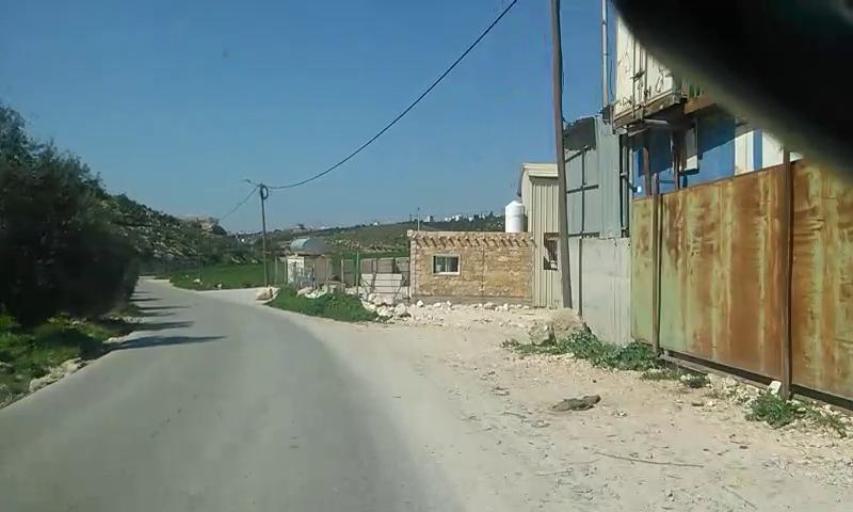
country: PS
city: Bayt Maqdum
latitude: 31.5396
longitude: 34.9724
